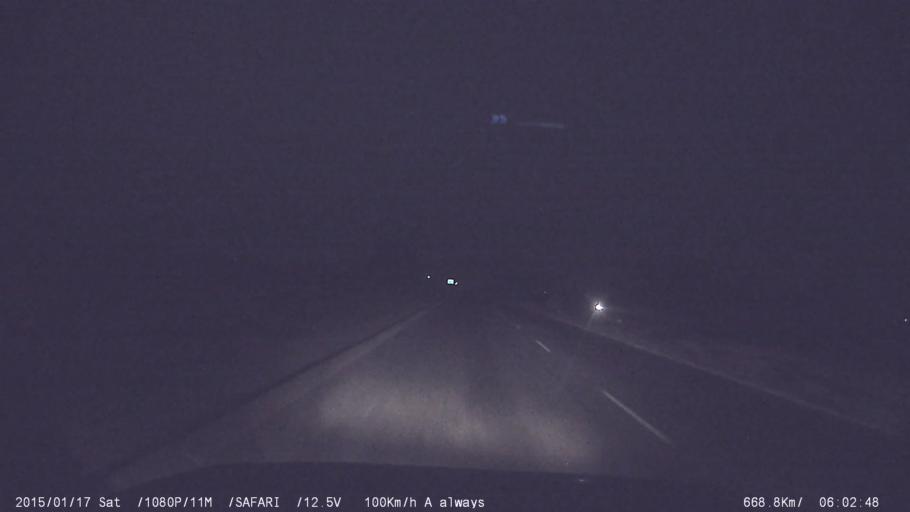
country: IN
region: Tamil Nadu
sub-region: Kancheepuram
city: Kanchipuram
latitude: 12.8870
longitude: 79.5964
